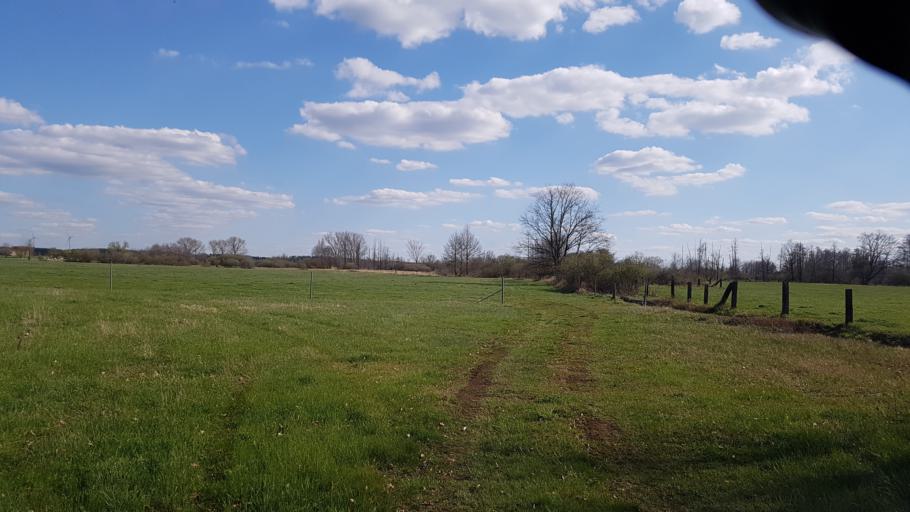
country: DE
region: Brandenburg
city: Falkenberg
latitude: 51.5076
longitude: 13.2698
